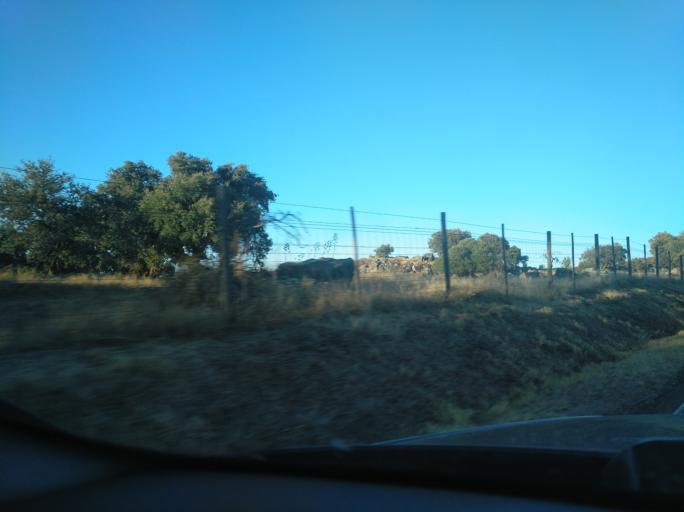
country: PT
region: Portalegre
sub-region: Arronches
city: Arronches
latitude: 39.0679
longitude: -7.2161
